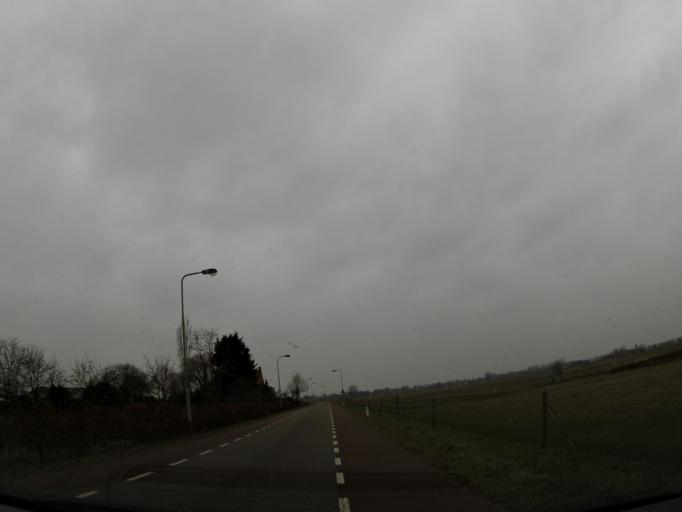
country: NL
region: Limburg
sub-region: Gemeente Maasgouw
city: Maasbracht
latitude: 51.1263
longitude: 5.8379
